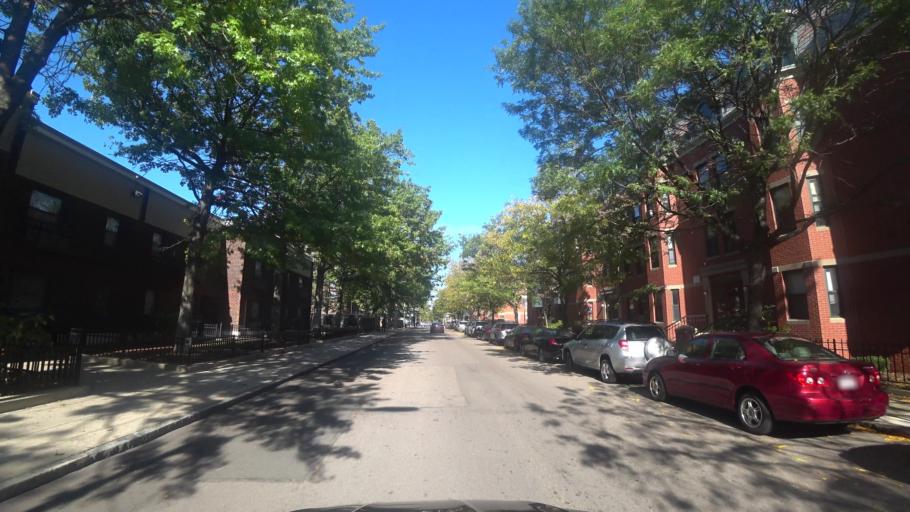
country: US
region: Massachusetts
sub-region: Suffolk County
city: South Boston
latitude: 42.3351
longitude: -71.0765
